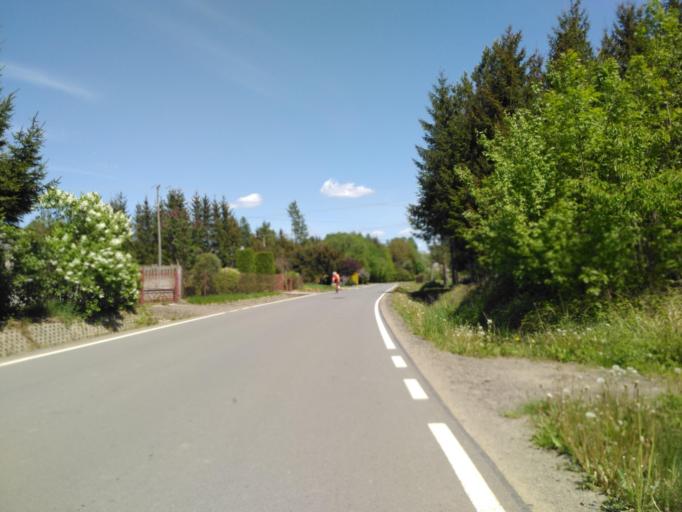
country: PL
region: Subcarpathian Voivodeship
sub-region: Powiat krosnienski
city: Dukla
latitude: 49.5969
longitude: 21.7028
